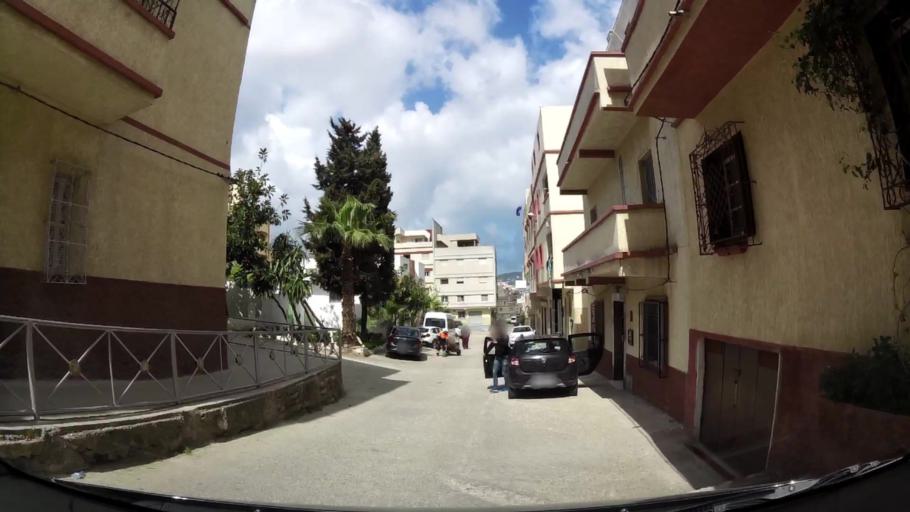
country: MA
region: Tanger-Tetouan
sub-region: Tanger-Assilah
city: Tangier
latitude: 35.7590
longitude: -5.8162
